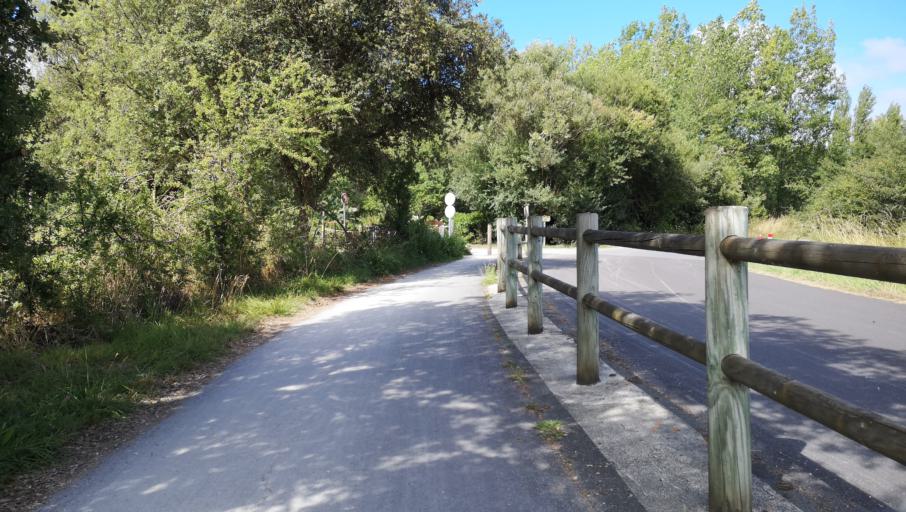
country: FR
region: Pays de la Loire
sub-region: Departement de la Vendee
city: Olonne-sur-Mer
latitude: 46.5277
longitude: -1.8063
